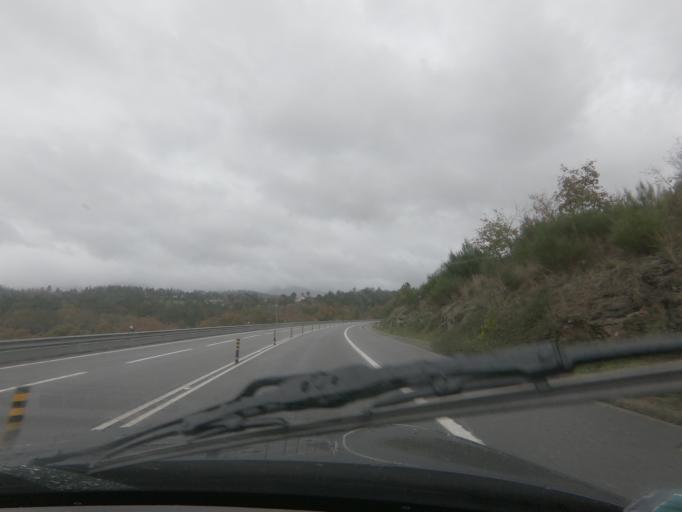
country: PT
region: Vila Real
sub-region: Santa Marta de Penaguiao
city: Santa Marta de Penaguiao
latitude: 41.2838
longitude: -7.8227
